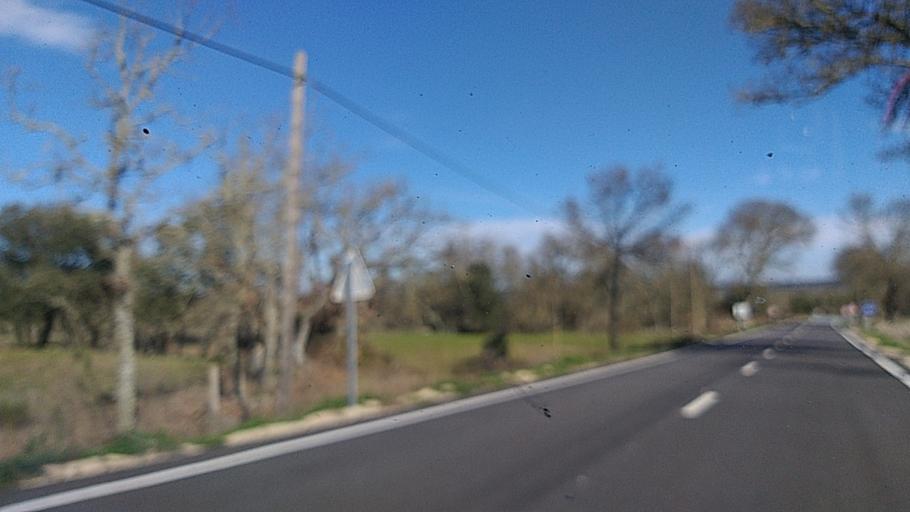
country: ES
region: Castille and Leon
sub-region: Provincia de Salamanca
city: Fuentes de Onoro
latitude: 40.5995
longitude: -6.9403
